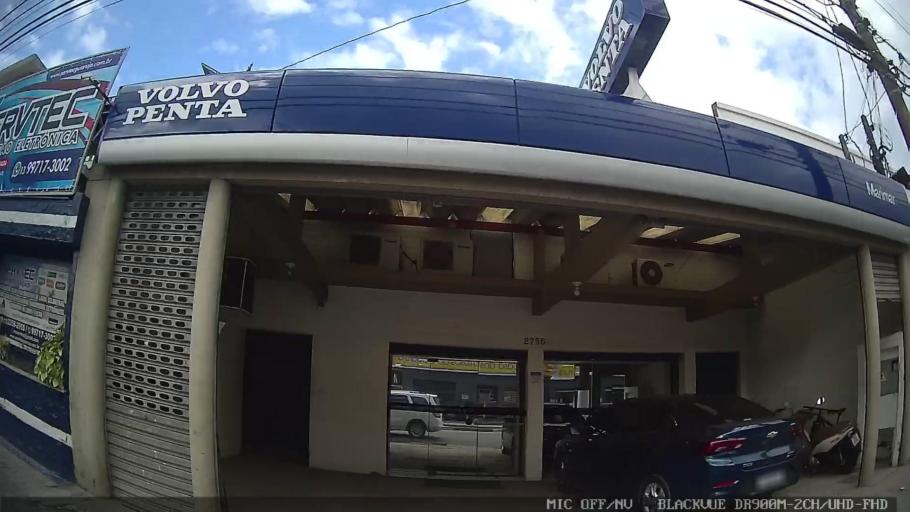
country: BR
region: Sao Paulo
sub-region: Guaruja
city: Guaruja
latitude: -23.9905
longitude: -46.2841
